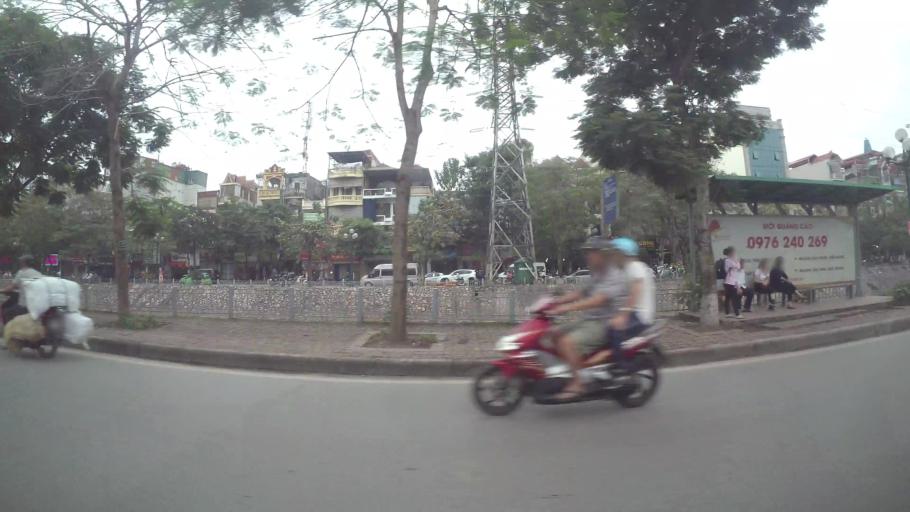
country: VN
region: Ha Noi
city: Hai BaTrung
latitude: 21.0056
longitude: 105.8610
